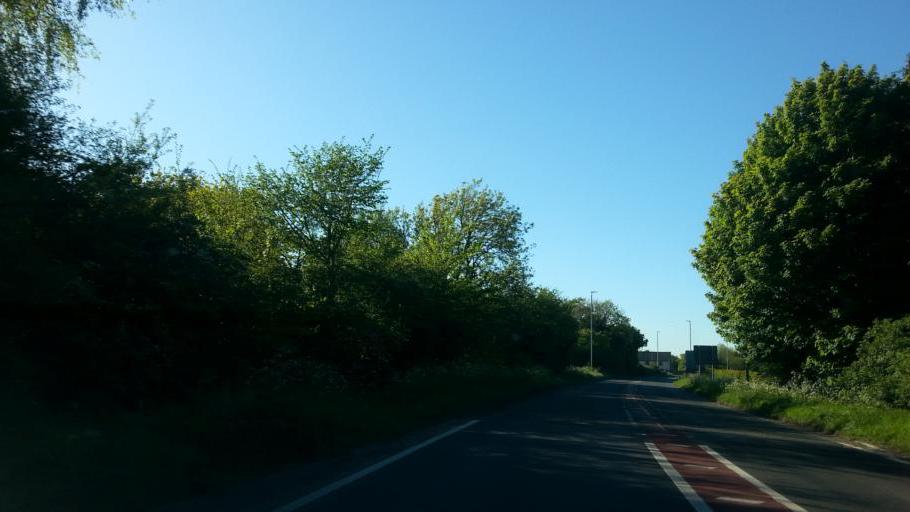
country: GB
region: England
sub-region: Somerset
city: Chilcompton
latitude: 51.2597
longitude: -2.5406
